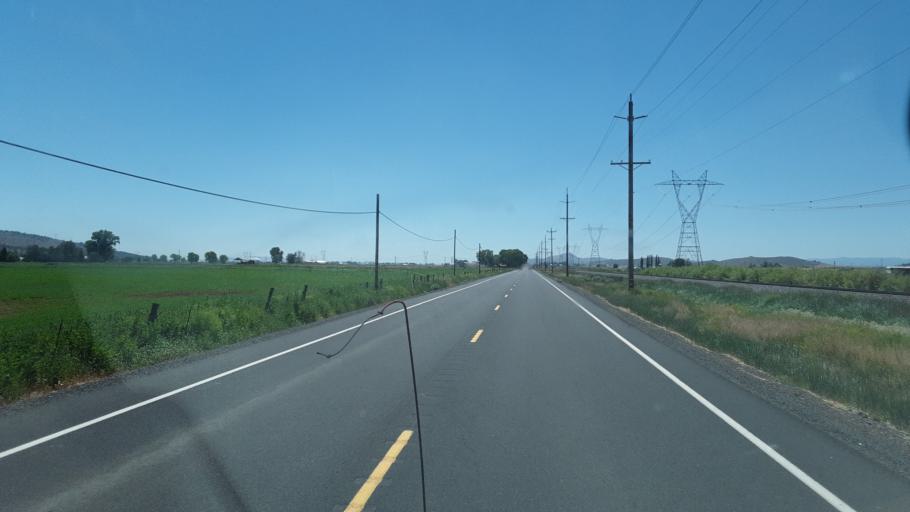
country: US
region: Oregon
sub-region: Klamath County
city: Altamont
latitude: 42.0889
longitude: -121.6849
